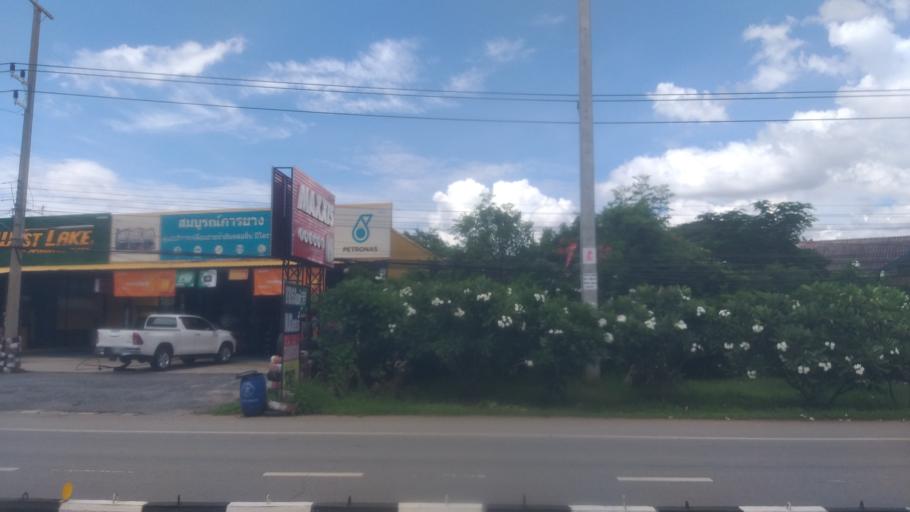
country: TH
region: Nakhon Ratchasima
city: Phra Thong Kham
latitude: 15.2626
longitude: 102.0239
